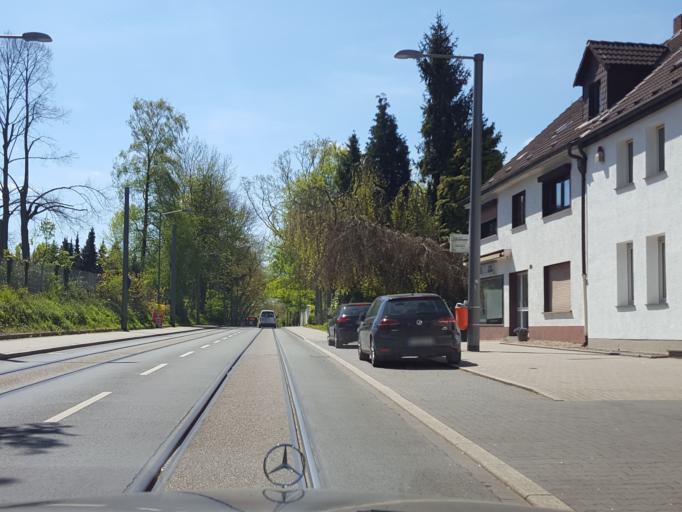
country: DE
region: North Rhine-Westphalia
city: Witten
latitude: 51.4701
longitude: 7.3235
